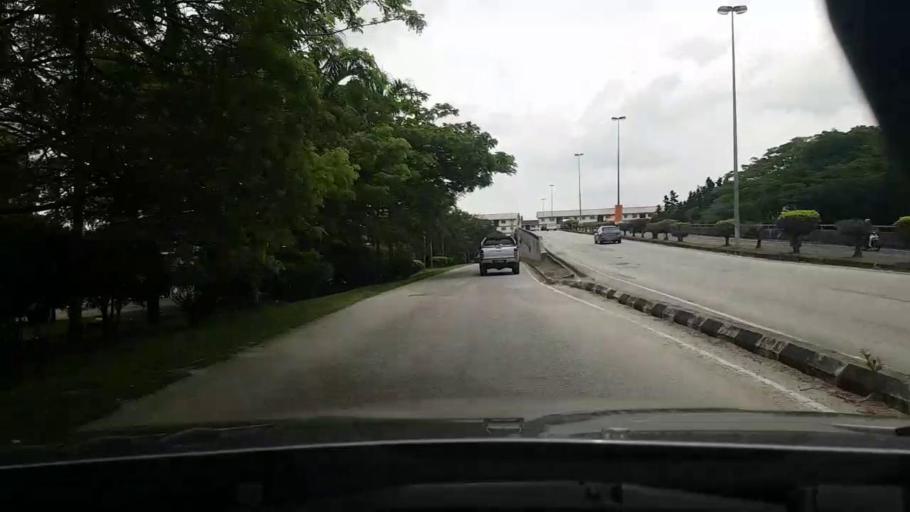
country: MY
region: Putrajaya
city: Putrajaya
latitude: 2.9828
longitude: 101.6313
